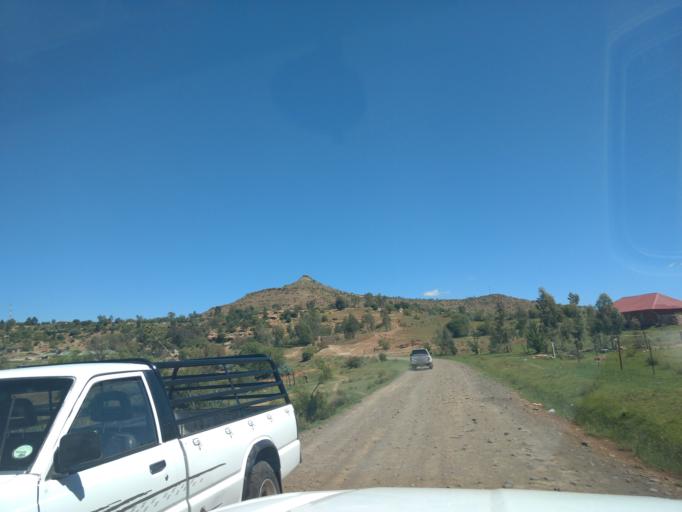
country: LS
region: Maseru
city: Maseru
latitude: -29.4894
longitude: 27.3708
